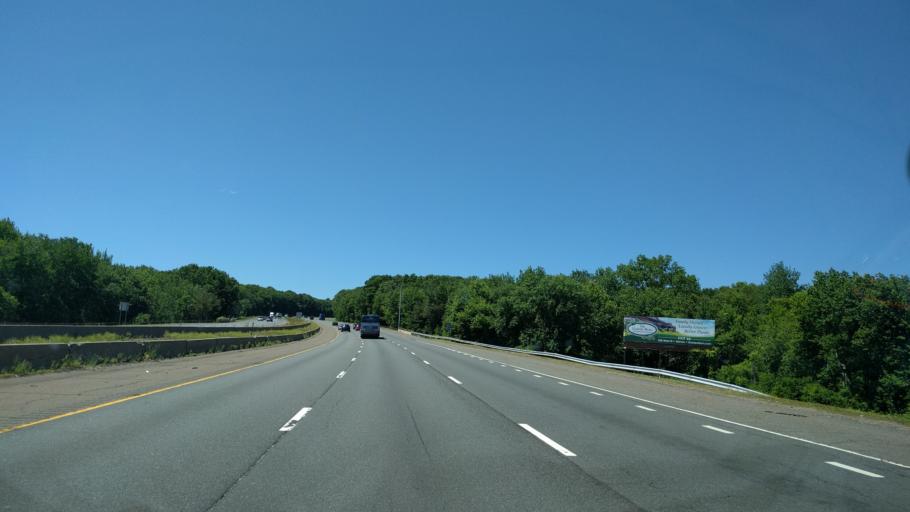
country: US
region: Connecticut
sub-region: Tolland County
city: Tolland
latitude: 41.8612
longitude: -72.3672
